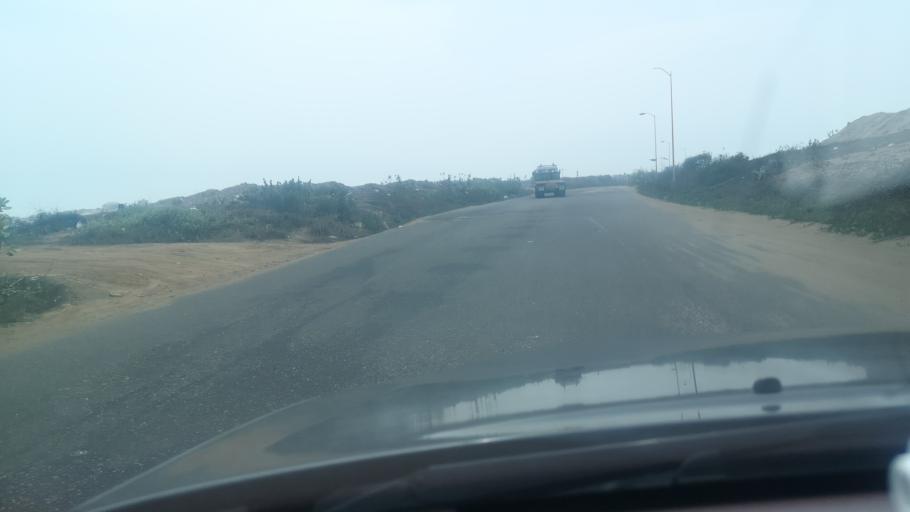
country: GH
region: Greater Accra
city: Nungua
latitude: 5.6103
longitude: -0.0508
